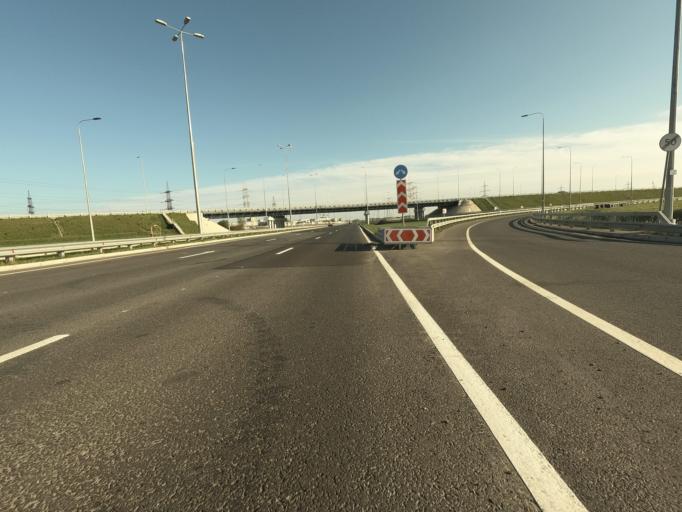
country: RU
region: St.-Petersburg
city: Kolpino
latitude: 59.7441
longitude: 30.5395
